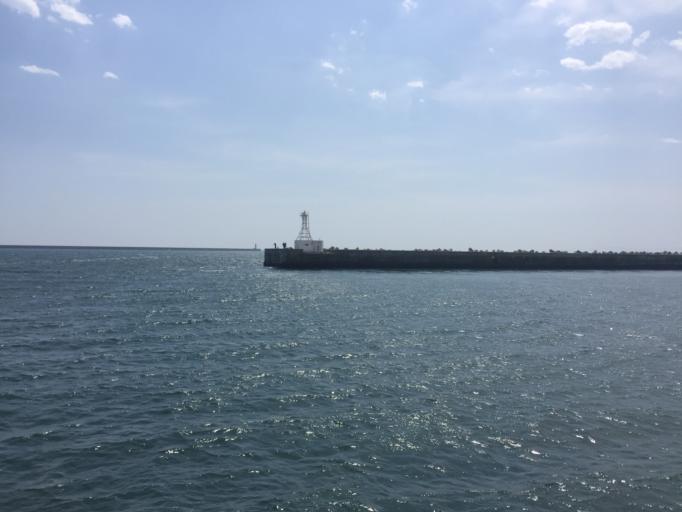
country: JP
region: Fukushima
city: Iwaki
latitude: 36.9221
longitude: 140.8850
